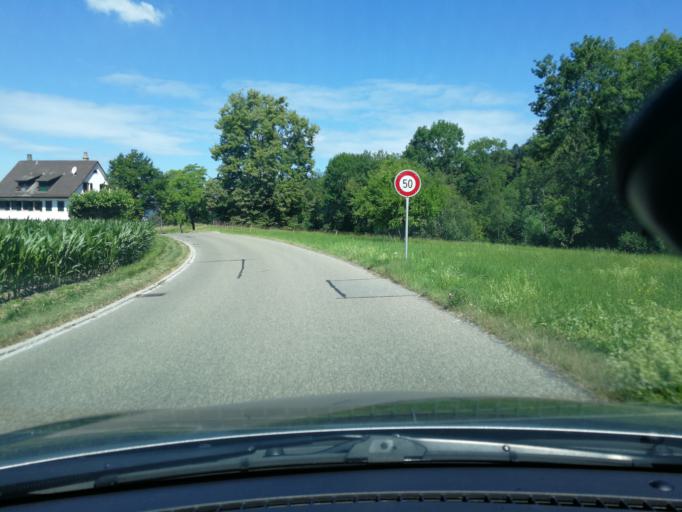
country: CH
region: Zurich
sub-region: Bezirk Meilen
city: Herrliberg
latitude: 47.3007
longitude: 8.6157
